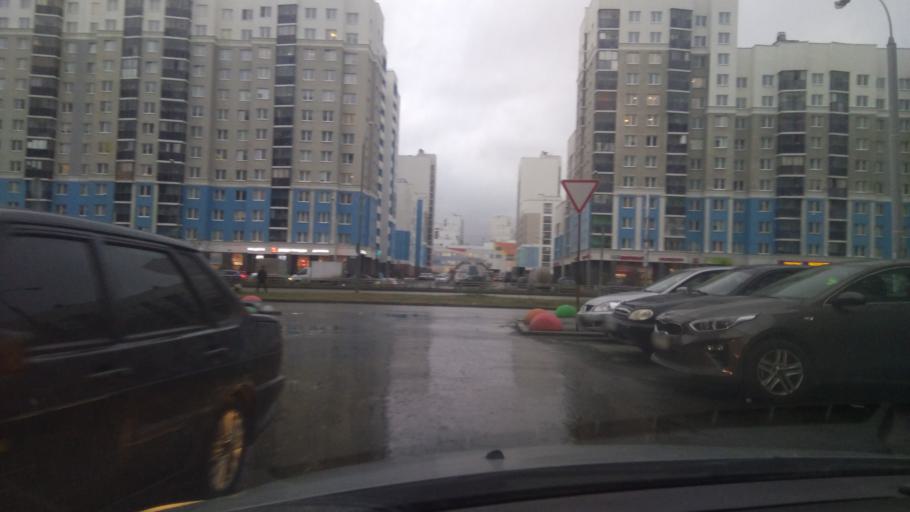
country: RU
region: Sverdlovsk
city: Shirokaya Rechka
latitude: 56.7901
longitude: 60.5174
